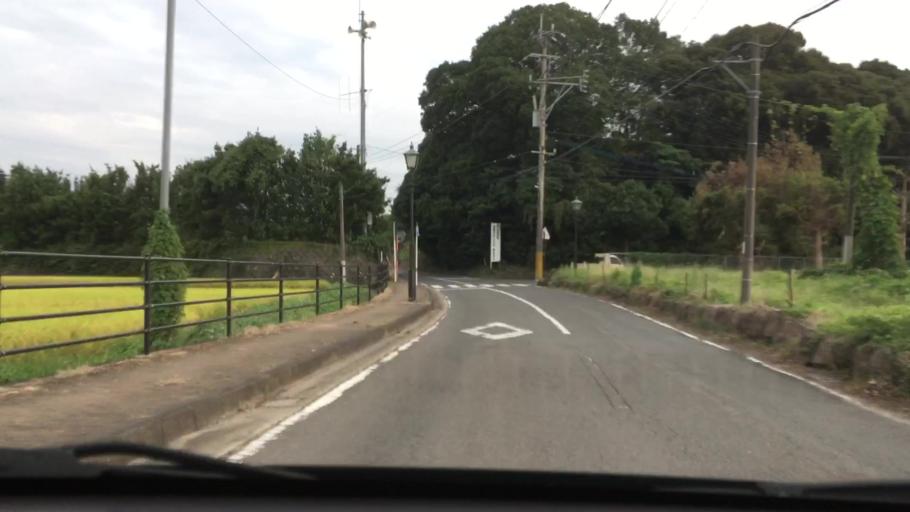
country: JP
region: Nagasaki
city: Sasebo
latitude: 32.9993
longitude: 129.7672
